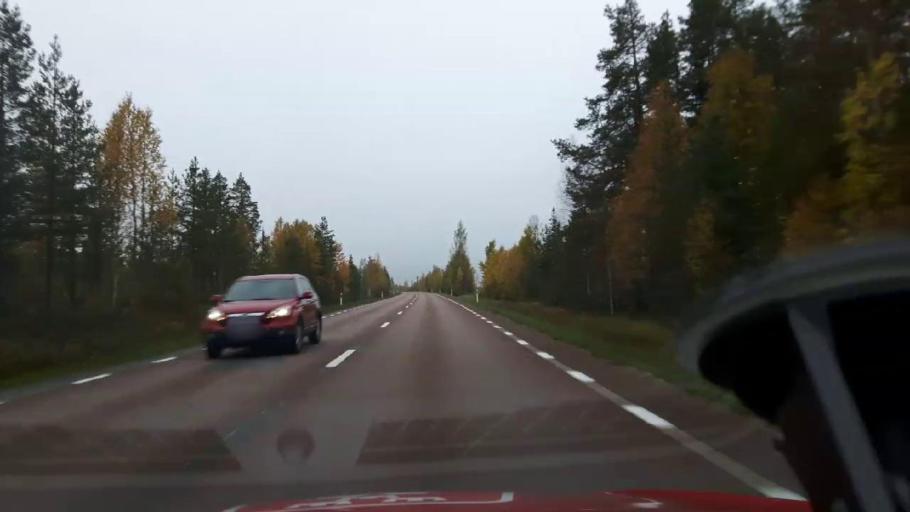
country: SE
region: Jaemtland
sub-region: Bergs Kommun
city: Hoverberg
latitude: 62.5354
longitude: 14.4479
